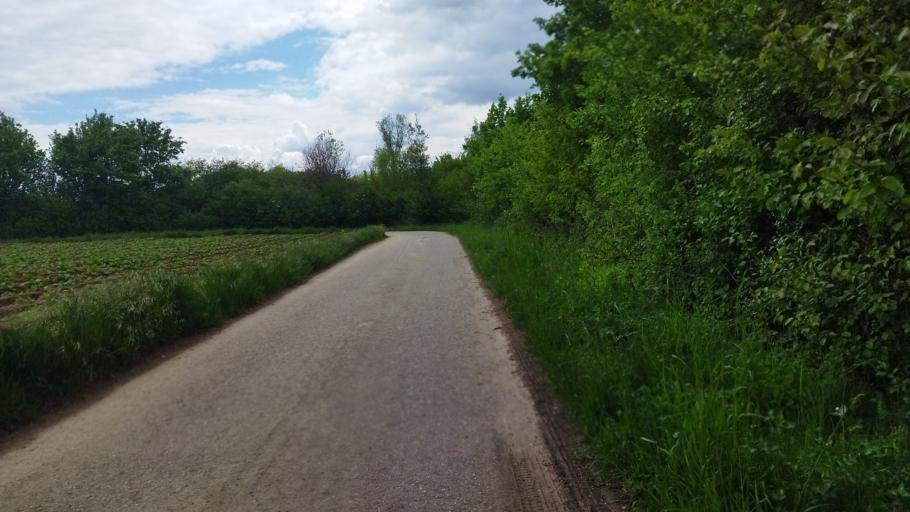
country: DE
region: Baden-Wuerttemberg
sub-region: Regierungsbezirk Stuttgart
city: Neckarwestheim
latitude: 49.0445
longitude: 9.1793
